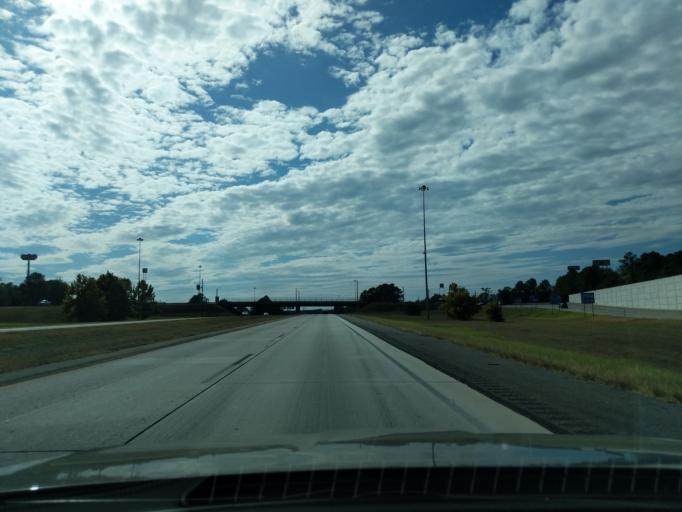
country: US
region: Georgia
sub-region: Columbia County
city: Evans
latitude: 33.4833
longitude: -82.1282
